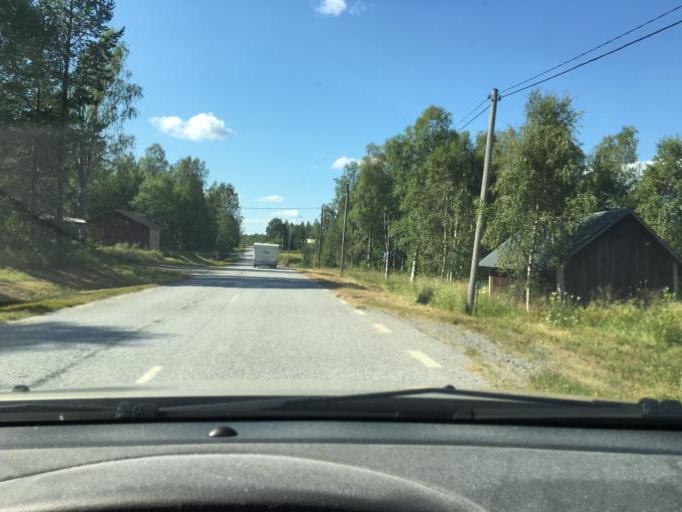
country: SE
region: Norrbotten
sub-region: Lulea Kommun
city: Ranea
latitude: 66.0453
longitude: 22.2865
